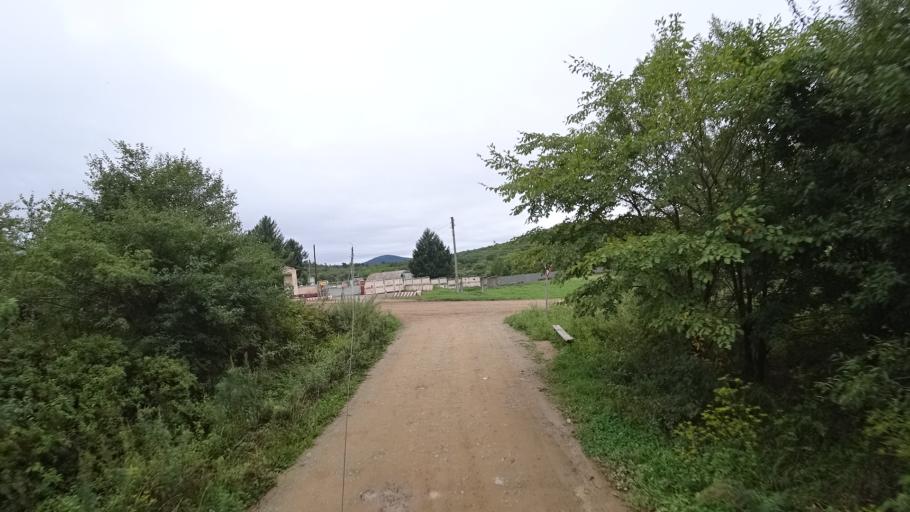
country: RU
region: Primorskiy
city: Rettikhovka
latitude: 44.1724
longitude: 132.8793
